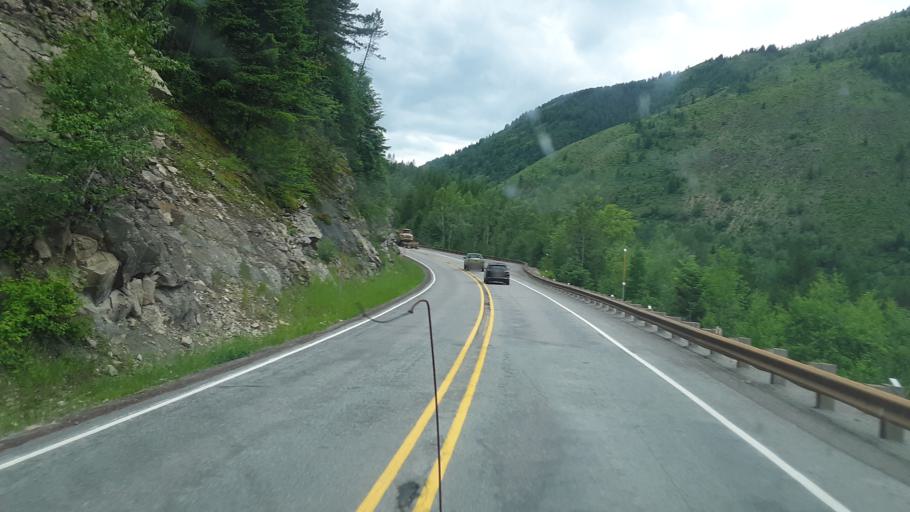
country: US
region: Montana
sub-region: Flathead County
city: Columbia Falls
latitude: 48.4942
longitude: -113.8845
